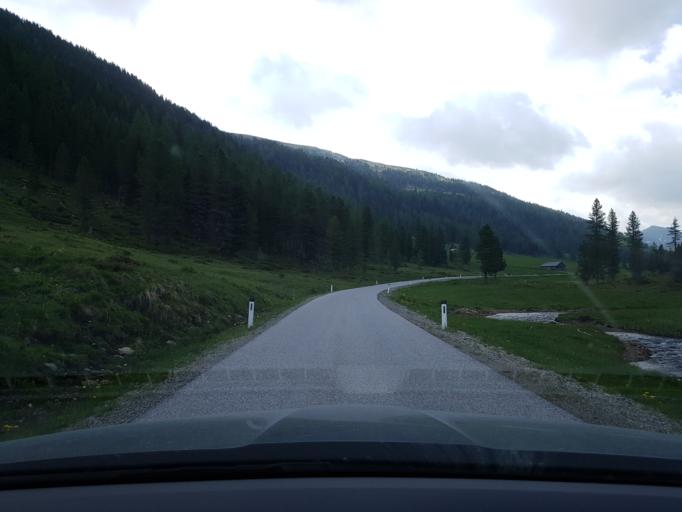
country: AT
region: Salzburg
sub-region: Politischer Bezirk Tamsweg
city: Thomatal
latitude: 47.0186
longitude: 13.7639
